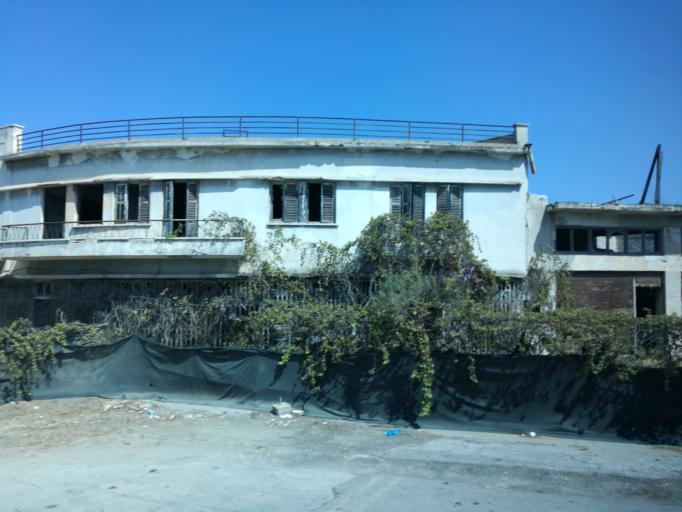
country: CY
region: Ammochostos
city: Famagusta
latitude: 35.1149
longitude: 33.9461
